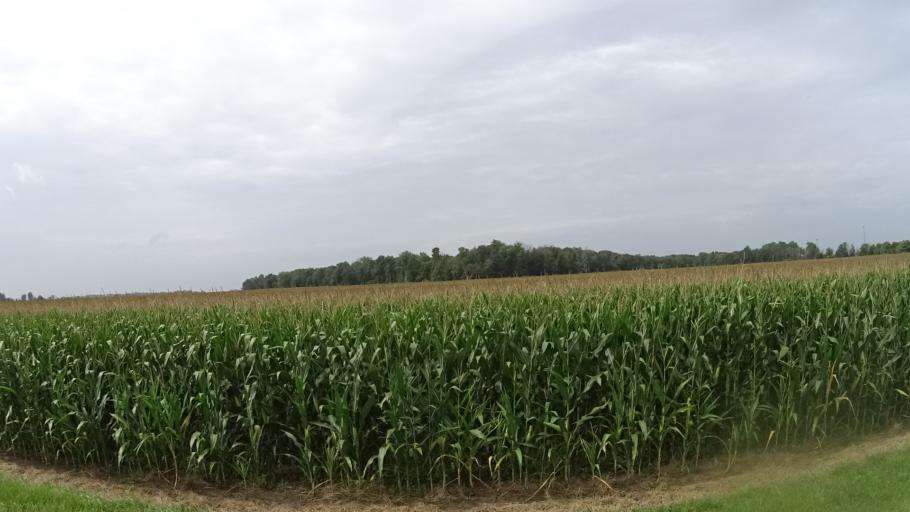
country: US
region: Indiana
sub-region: Madison County
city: Pendleton
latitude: 40.0229
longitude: -85.7748
